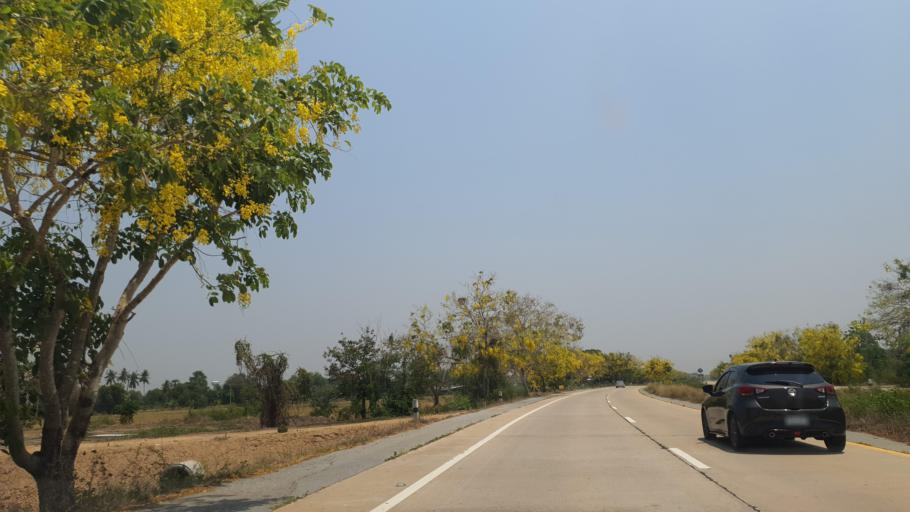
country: TH
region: Suphan Buri
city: Suphan Buri
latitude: 14.5213
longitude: 100.0550
